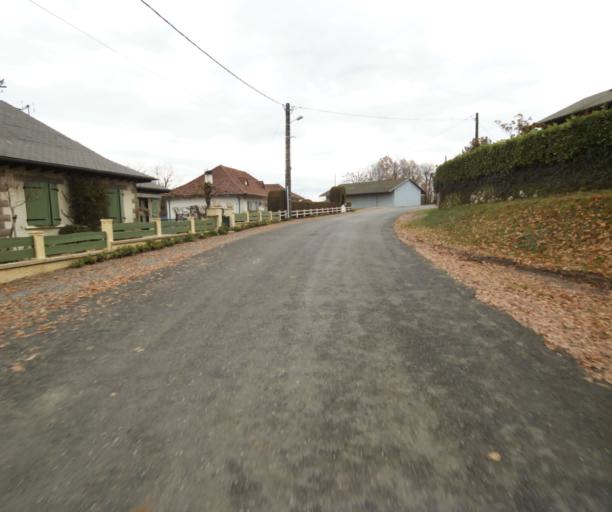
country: FR
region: Limousin
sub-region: Departement de la Correze
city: Tulle
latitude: 45.2515
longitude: 1.7334
